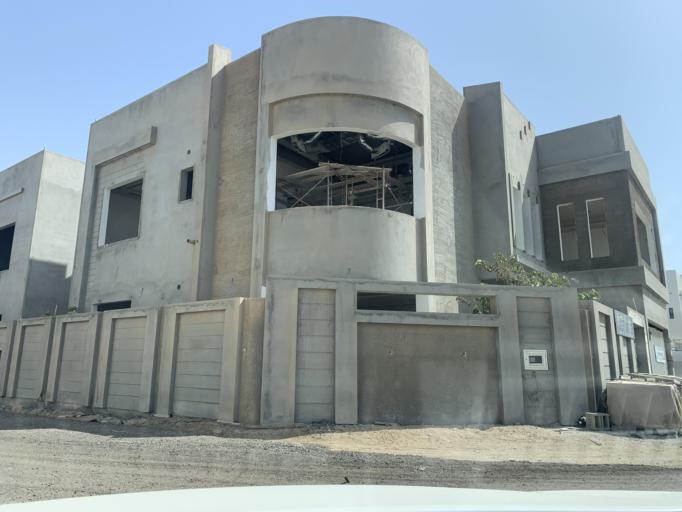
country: BH
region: Manama
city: Jidd Hafs
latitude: 26.2323
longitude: 50.4695
